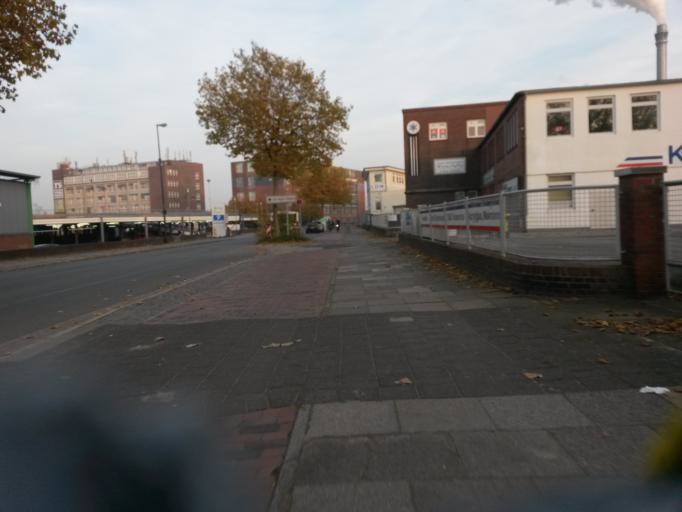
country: DE
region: Bremen
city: Bremen
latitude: 53.0619
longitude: 8.8690
